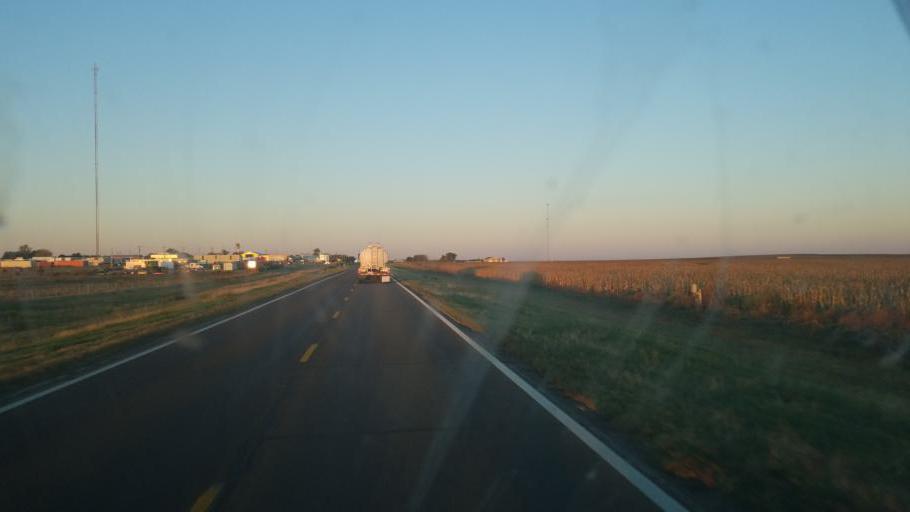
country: US
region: Kansas
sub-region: Wallace County
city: Sharon Springs
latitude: 38.9018
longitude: -101.7372
